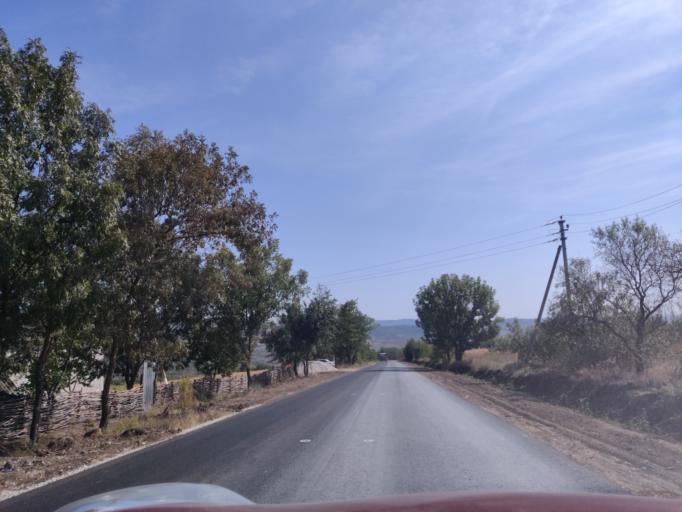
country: MD
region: Ungheni
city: Ungheni
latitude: 47.2625
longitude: 27.9811
